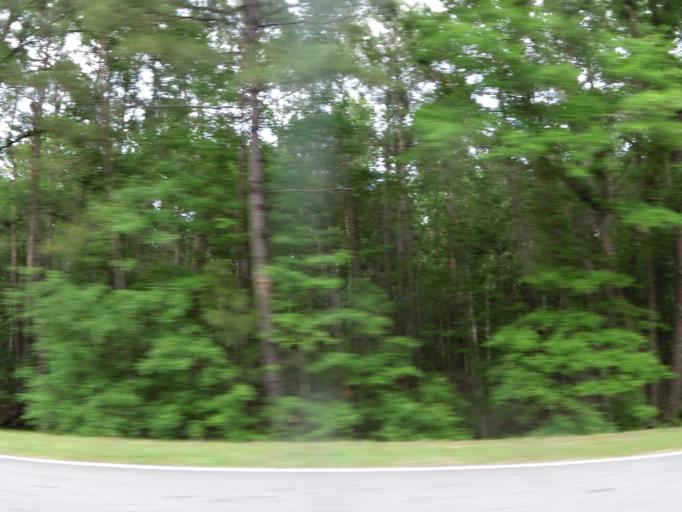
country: US
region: South Carolina
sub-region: Jasper County
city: Hardeeville
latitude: 32.3758
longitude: -81.0963
